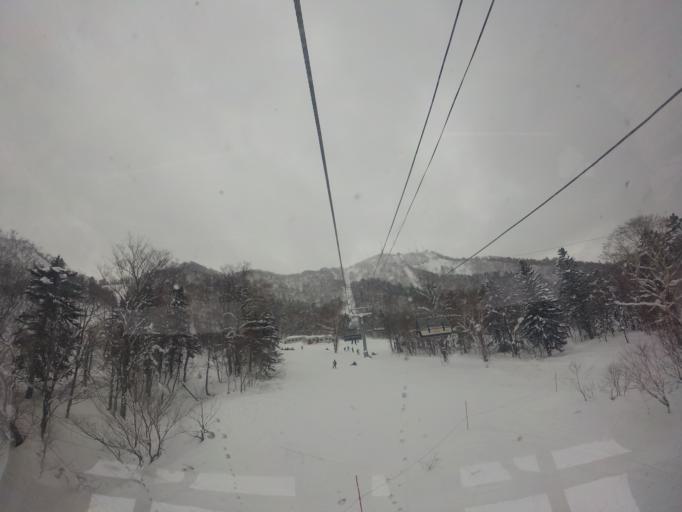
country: JP
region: Hokkaido
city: Sapporo
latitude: 43.0827
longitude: 141.2031
